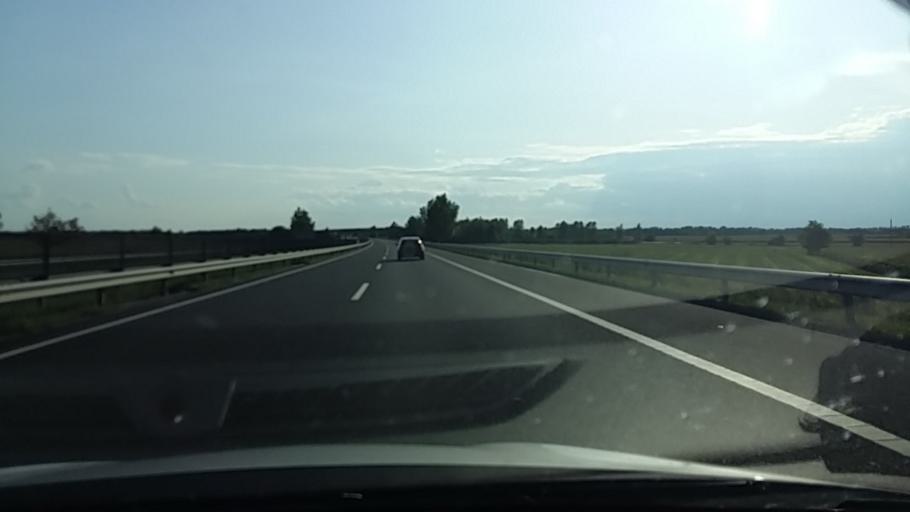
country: HU
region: Hajdu-Bihar
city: Hajdunanas
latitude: 47.8782
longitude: 21.3948
